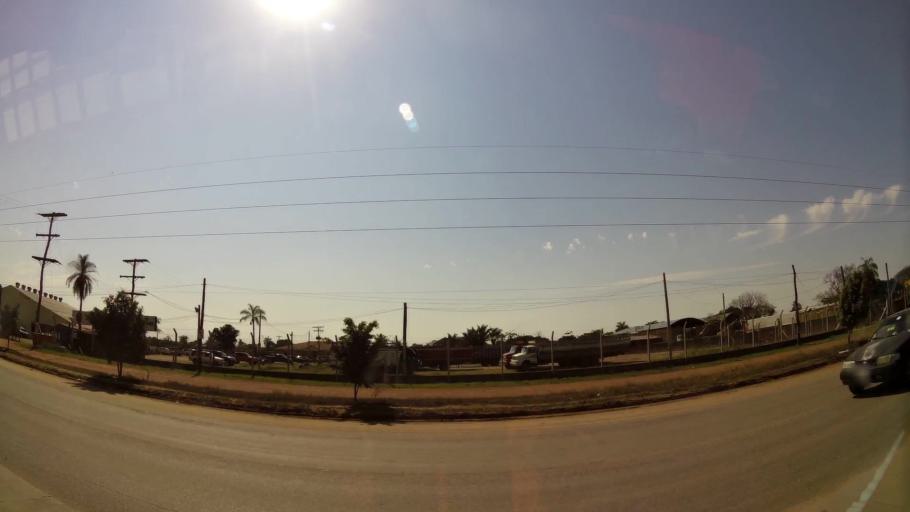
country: BO
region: Santa Cruz
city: Cotoca
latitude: -17.7649
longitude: -63.1035
